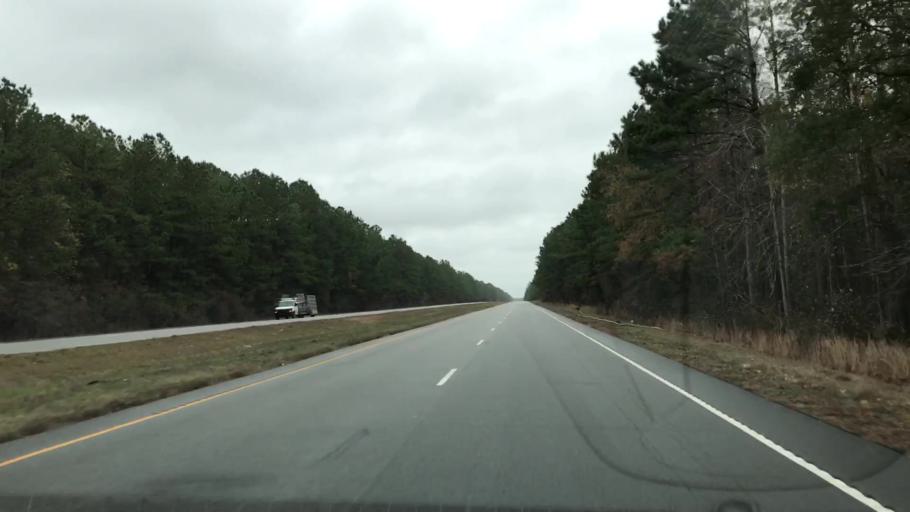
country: US
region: South Carolina
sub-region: Charleston County
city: Awendaw
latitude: 33.1492
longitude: -79.4339
